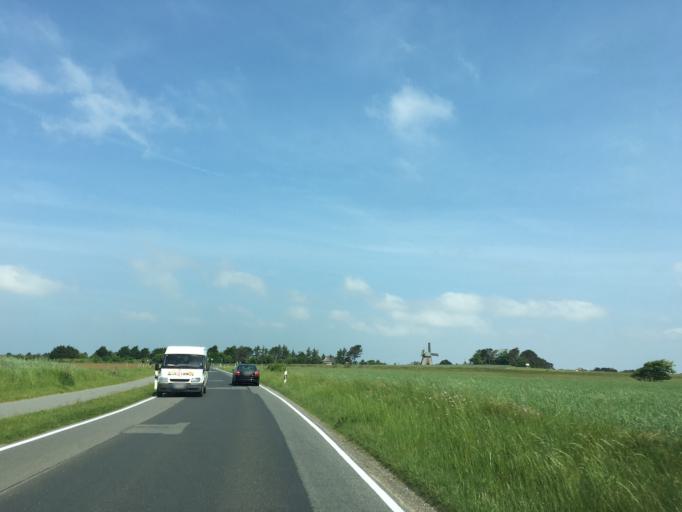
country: DE
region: Schleswig-Holstein
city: Nebel
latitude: 54.6448
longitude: 8.3545
